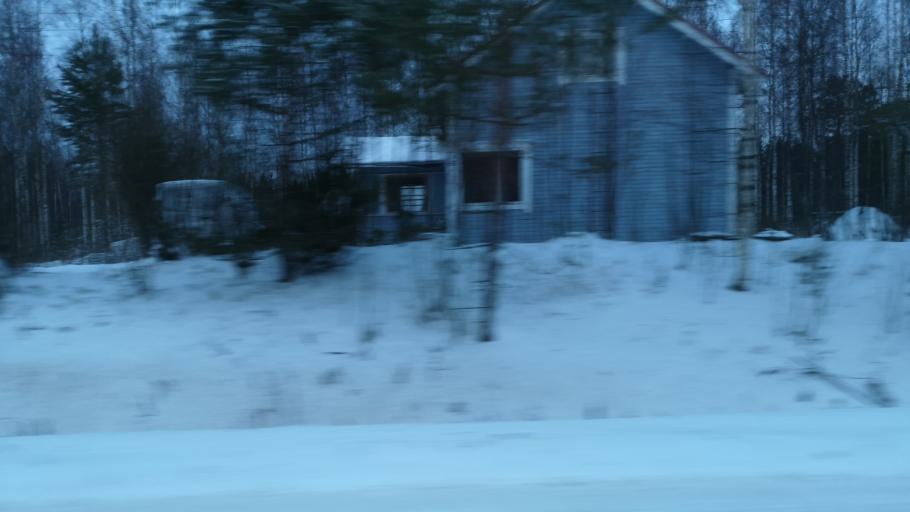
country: FI
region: Southern Savonia
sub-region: Savonlinna
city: Enonkoski
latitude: 62.1068
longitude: 28.6311
